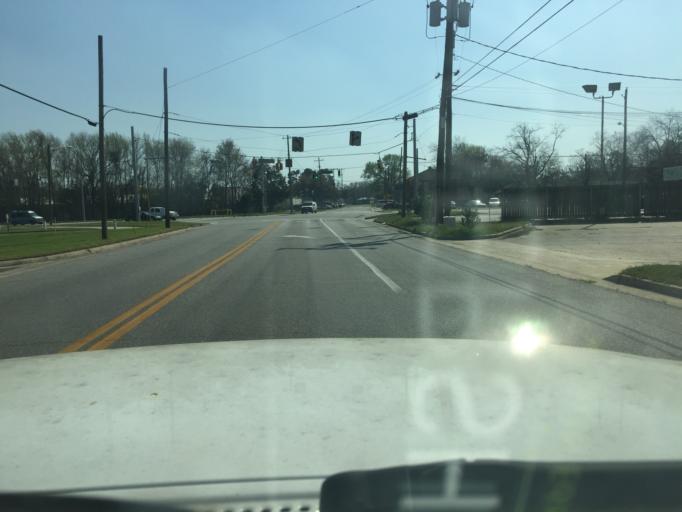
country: US
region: Georgia
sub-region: Chatham County
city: Savannah
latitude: 32.0871
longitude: -81.1115
